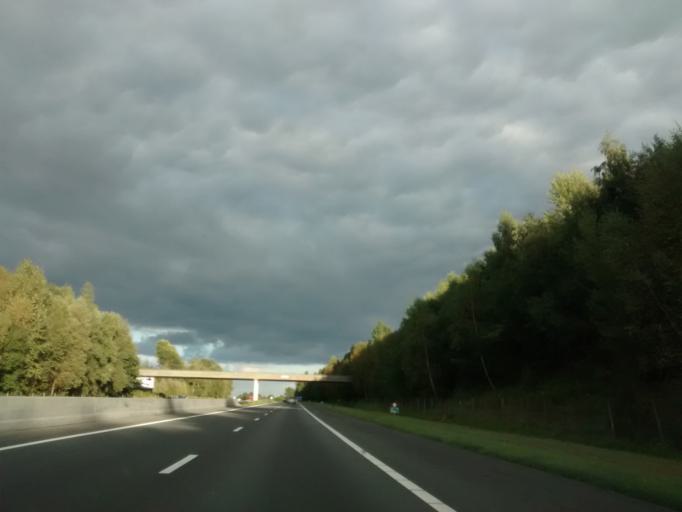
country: NL
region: Overijssel
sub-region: Gemeente Losser
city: Losser
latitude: 52.3081
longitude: 6.9937
